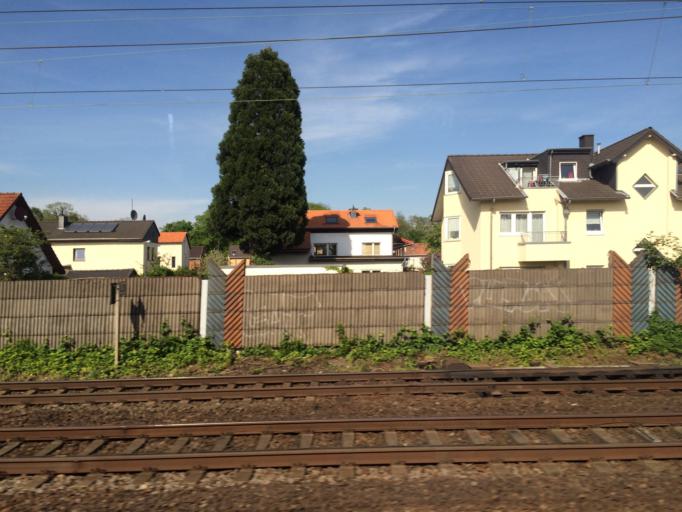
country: DE
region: North Rhine-Westphalia
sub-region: Regierungsbezirk Koln
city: Muelheim
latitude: 50.9823
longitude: 7.0069
